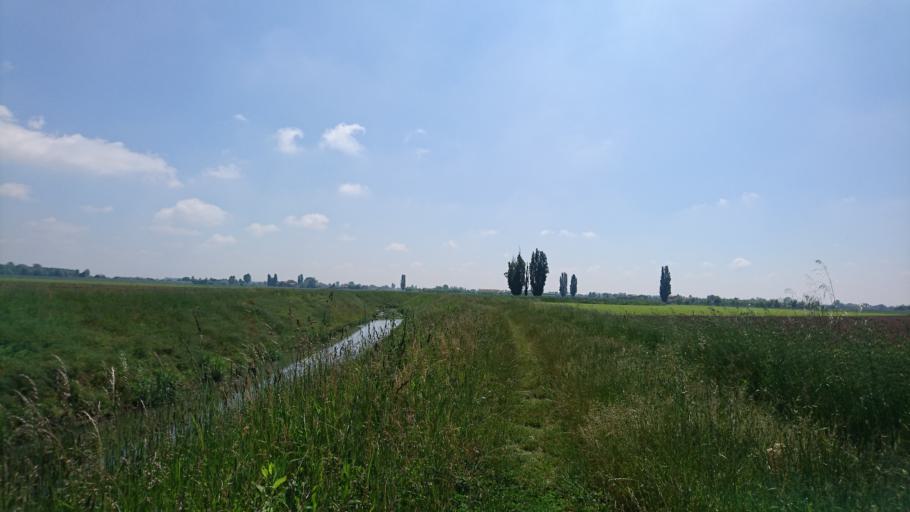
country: IT
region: Veneto
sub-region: Provincia di Padova
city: Casalserugo
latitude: 45.3378
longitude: 11.9228
